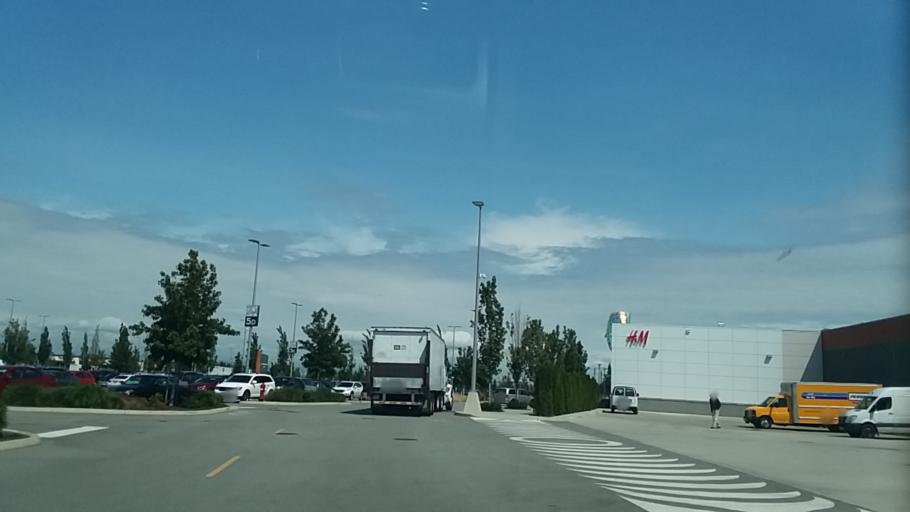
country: CA
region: British Columbia
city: Ladner
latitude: 49.0388
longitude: -123.0871
